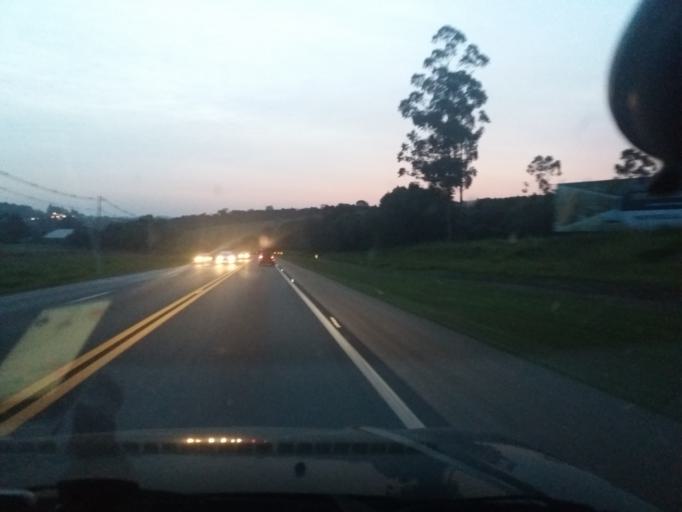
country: BR
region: Sao Paulo
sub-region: Itapeva
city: Itapeva
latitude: -23.9771
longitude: -48.8375
